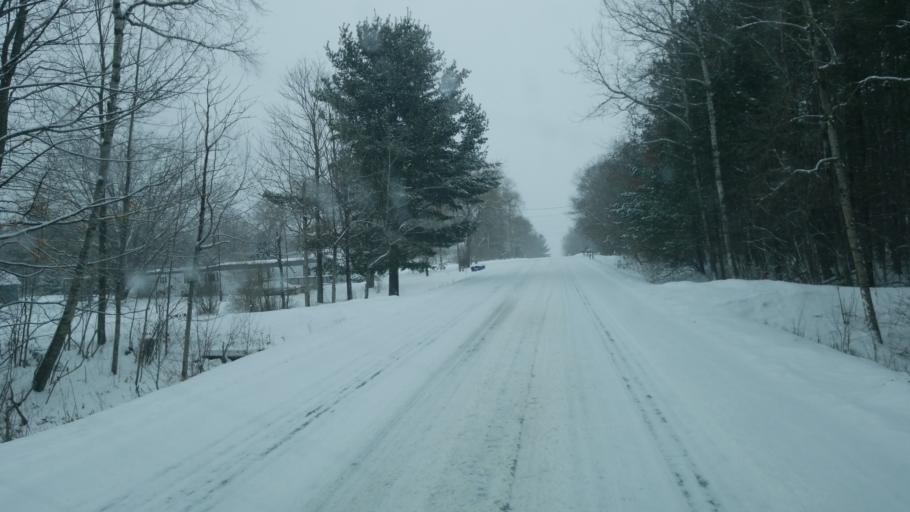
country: US
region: Michigan
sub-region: Mecosta County
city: Big Rapids
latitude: 43.5768
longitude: -85.4380
